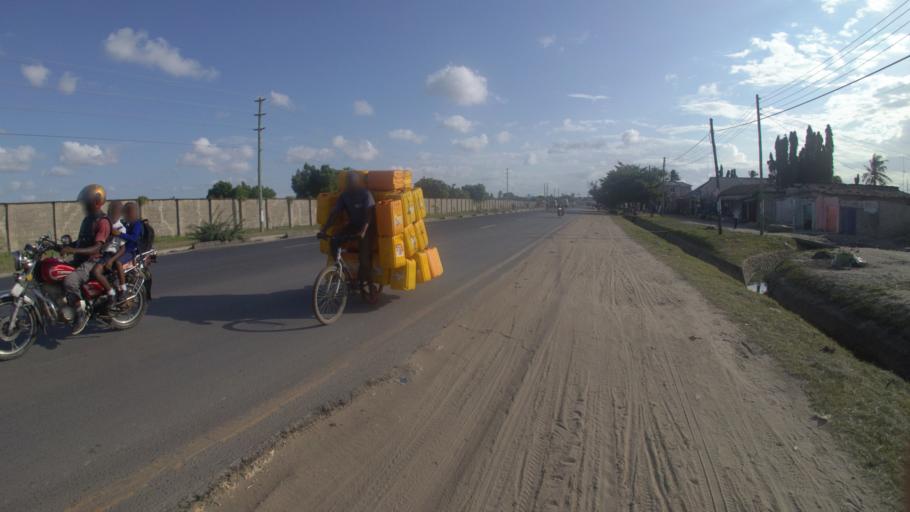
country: TZ
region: Dar es Salaam
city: Dar es Salaam
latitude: -6.8678
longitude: 39.1964
